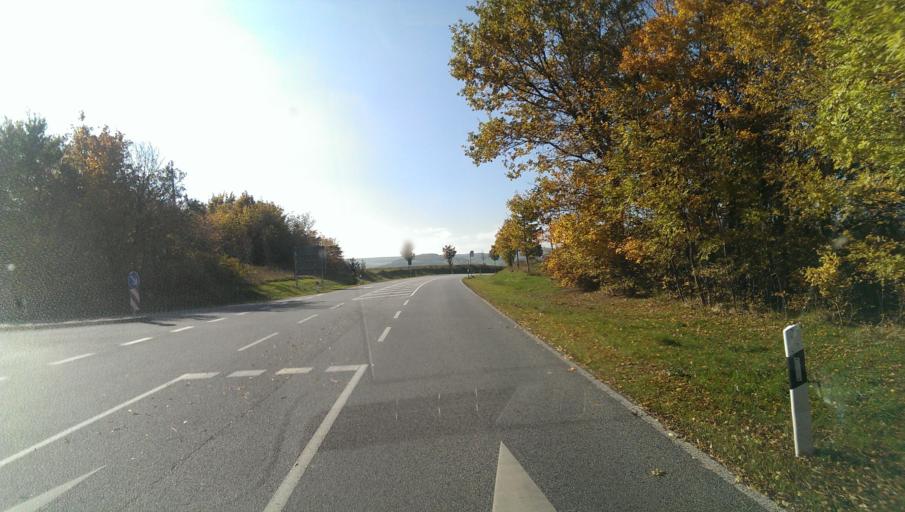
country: DE
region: Saxony
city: Barenstein
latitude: 50.7821
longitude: 13.8519
